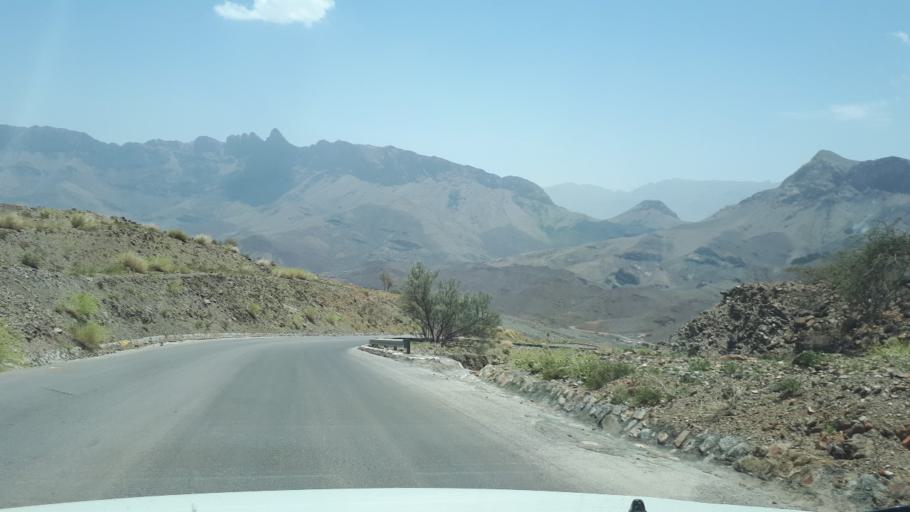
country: OM
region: Muhafazat ad Dakhiliyah
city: Bahla'
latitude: 23.2077
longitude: 57.1467
